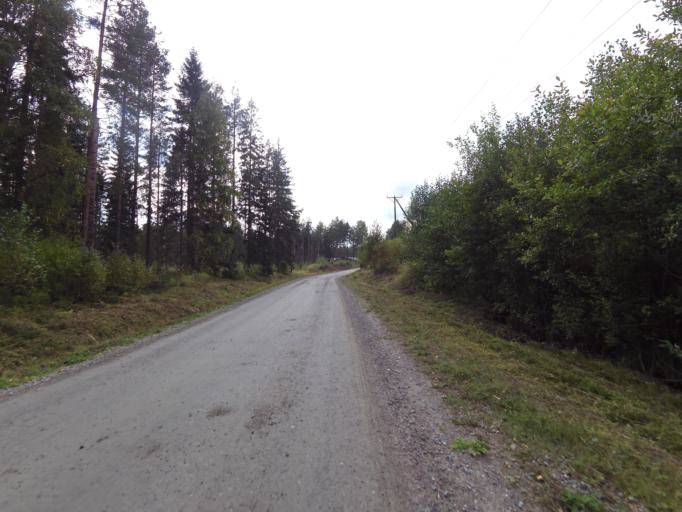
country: SE
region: Gaevleborg
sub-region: Sandvikens Kommun
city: Sandviken
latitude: 60.7162
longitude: 16.8090
